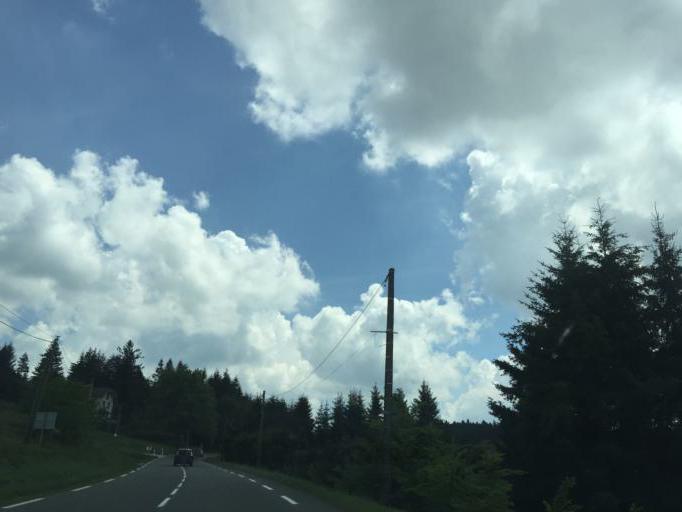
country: FR
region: Rhone-Alpes
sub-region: Departement de la Loire
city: Saint-Genest-Malifaux
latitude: 45.3742
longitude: 4.4454
